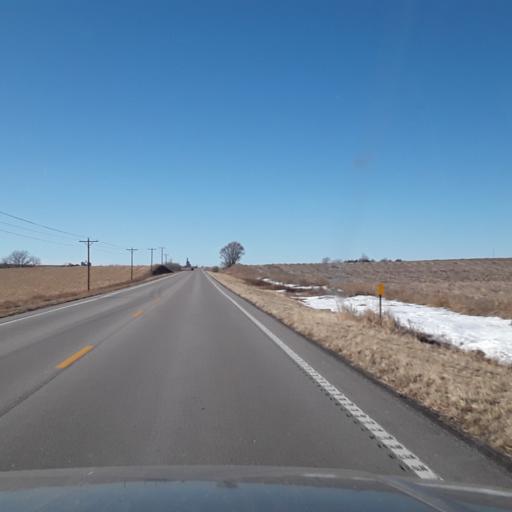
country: US
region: Nebraska
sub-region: Dawson County
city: Gothenburg
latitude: 40.7039
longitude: -100.1754
